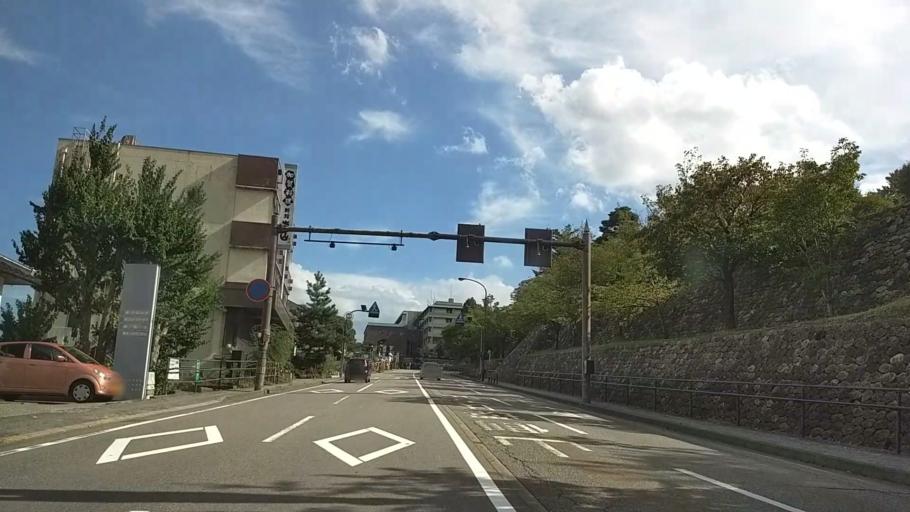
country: JP
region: Ishikawa
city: Kanazawa-shi
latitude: 36.5634
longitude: 136.6638
